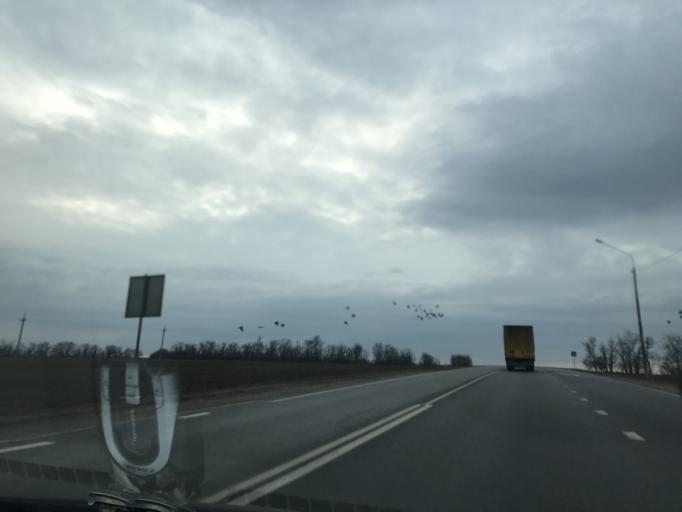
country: RU
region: Krasnodarskiy
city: Alekseyevskaya
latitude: 45.7902
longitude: 40.2230
